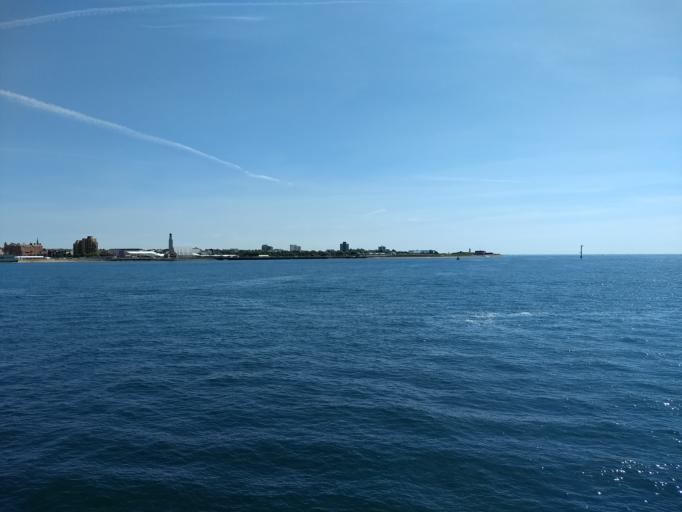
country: GB
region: England
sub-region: Portsmouth
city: Southsea
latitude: 50.7804
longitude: -1.1045
